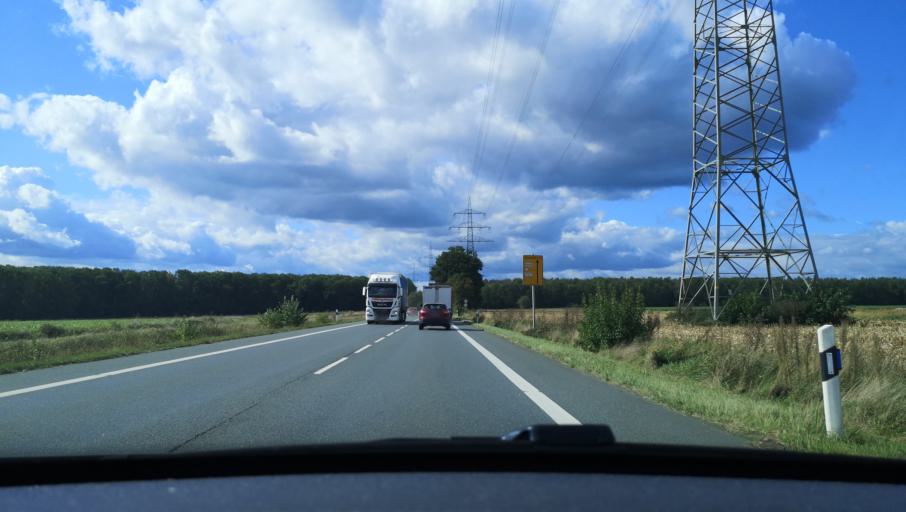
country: DE
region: Hesse
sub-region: Regierungsbezirk Darmstadt
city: Rodgau
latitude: 50.0155
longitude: 8.8594
